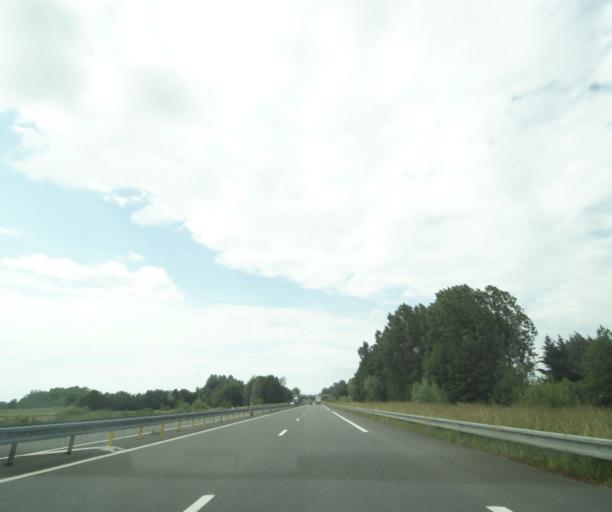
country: FR
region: Pays de la Loire
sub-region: Departement de Maine-et-Loire
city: Brion
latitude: 47.4580
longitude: -0.1811
